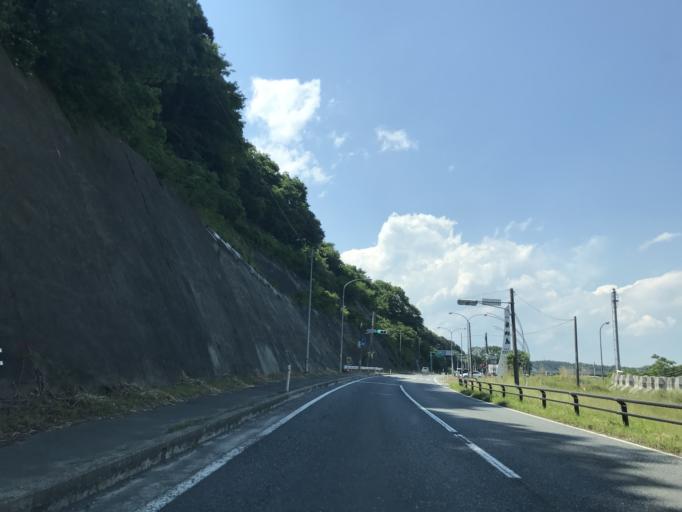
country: JP
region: Miyagi
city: Yamoto
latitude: 38.4056
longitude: 141.1473
